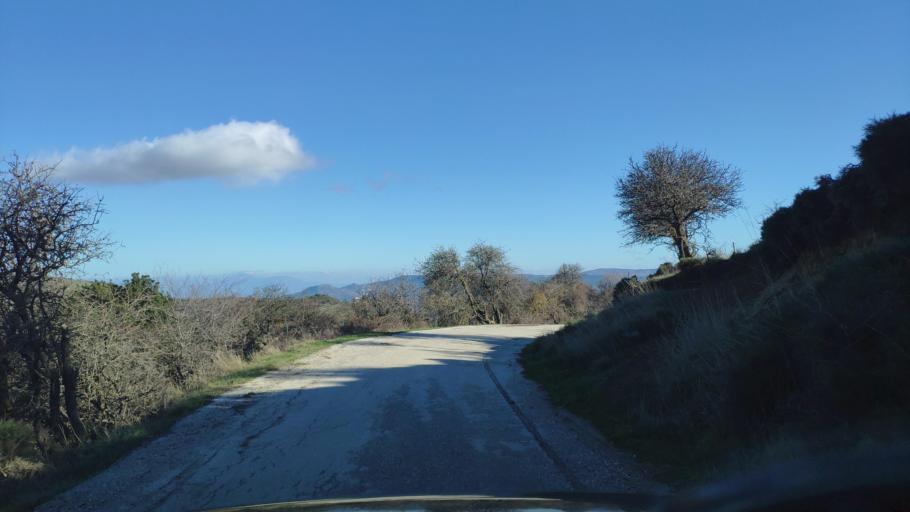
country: GR
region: West Greece
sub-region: Nomos Achaias
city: Aiyira
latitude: 38.0390
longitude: 22.4658
